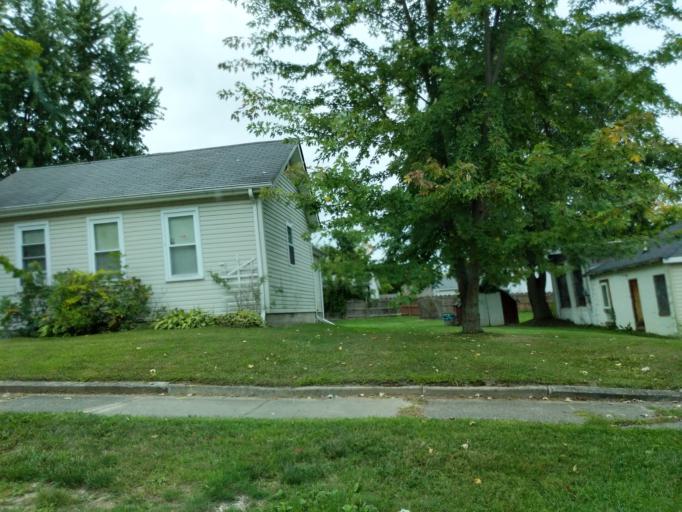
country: US
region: Michigan
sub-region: Tuscola County
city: Caro
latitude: 43.3365
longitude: -83.3539
